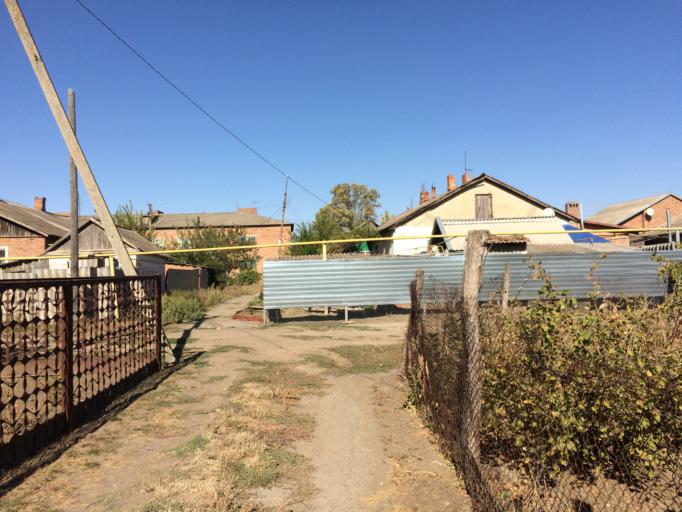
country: RU
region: Rostov
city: Tselina
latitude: 46.5149
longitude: 41.1843
